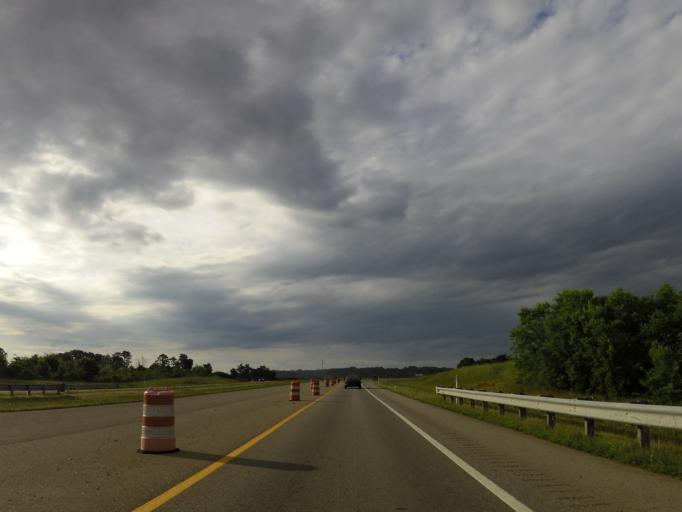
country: US
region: Tennessee
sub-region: Blount County
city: Eagleton Village
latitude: 35.8092
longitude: -83.9438
